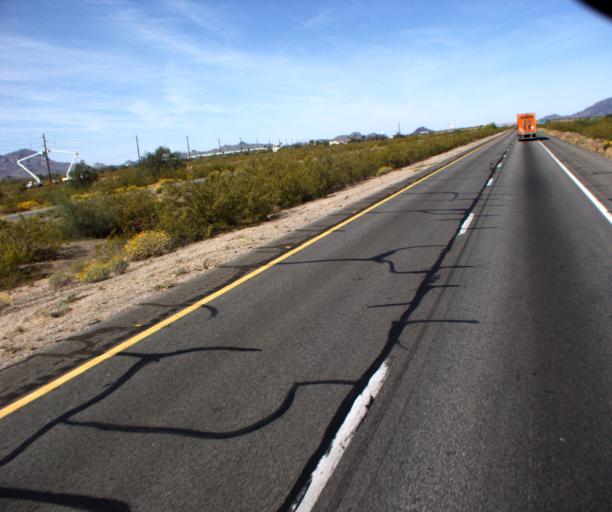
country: US
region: Arizona
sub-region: Maricopa County
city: Buckeye
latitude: 33.4948
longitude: -112.9247
